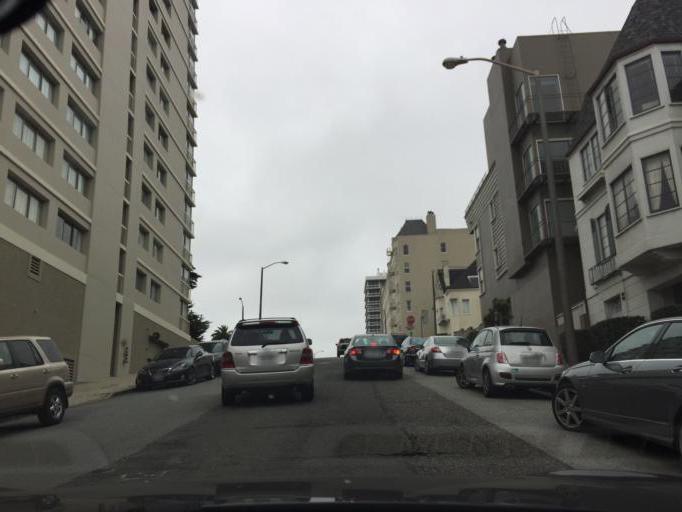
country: US
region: California
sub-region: San Francisco County
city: San Francisco
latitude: 37.7928
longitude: -122.4296
